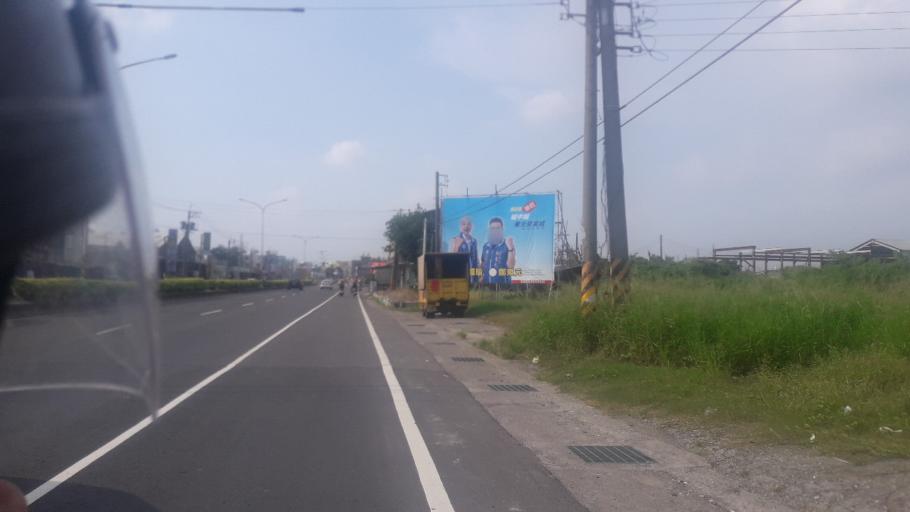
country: TW
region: Taiwan
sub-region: Tainan
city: Tainan
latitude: 22.8746
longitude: 120.2538
